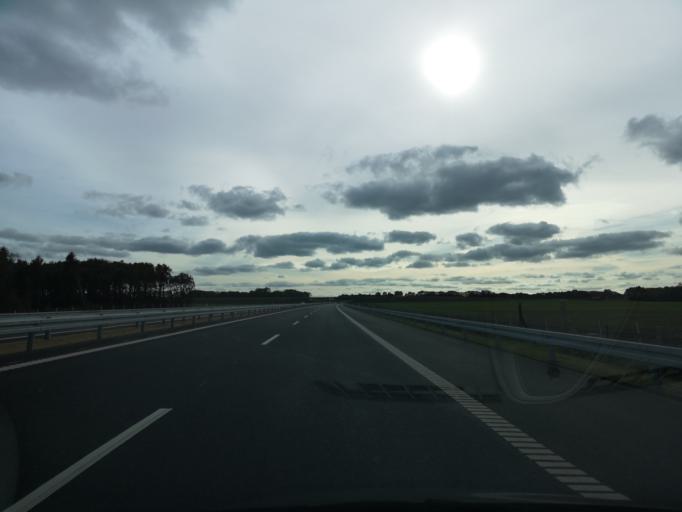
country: DK
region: Central Jutland
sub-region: Herning Kommune
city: Avlum
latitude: 56.3223
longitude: 8.7332
